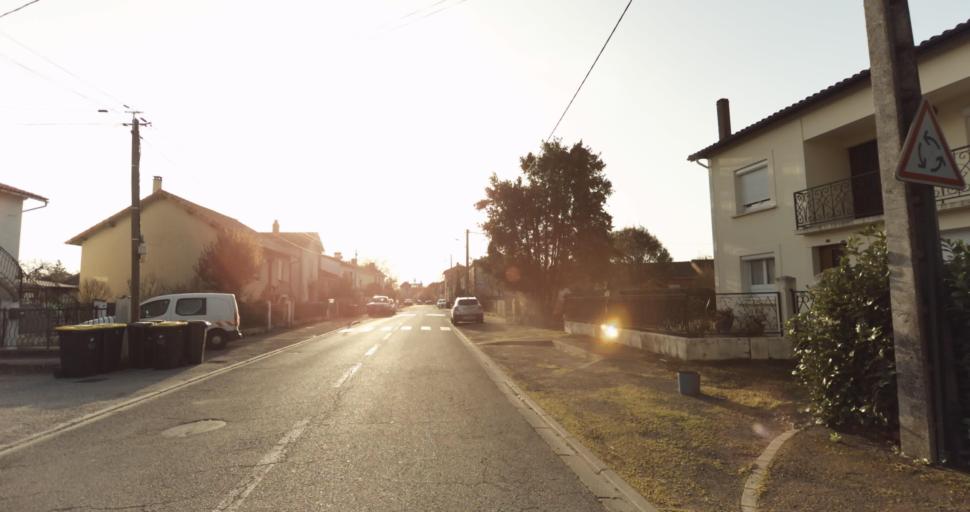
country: FR
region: Midi-Pyrenees
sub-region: Departement du Tarn
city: Saint-Sulpice-la-Pointe
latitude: 43.7772
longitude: 1.6780
